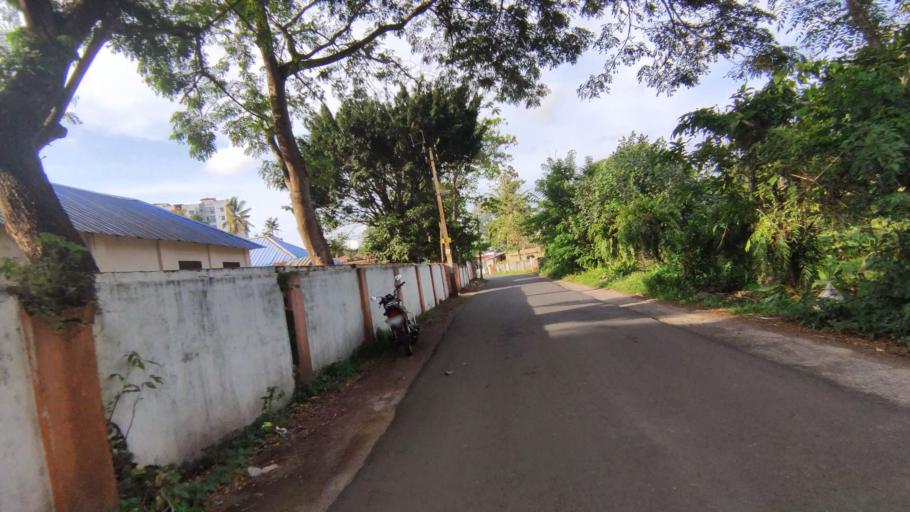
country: IN
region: Kerala
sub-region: Kottayam
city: Kottayam
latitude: 9.5789
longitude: 76.4991
